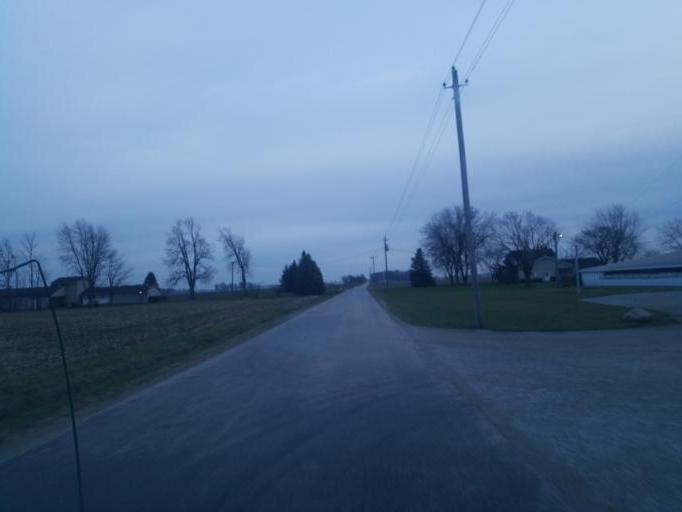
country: US
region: Indiana
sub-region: Adams County
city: Decatur
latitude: 40.7597
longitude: -85.0140
